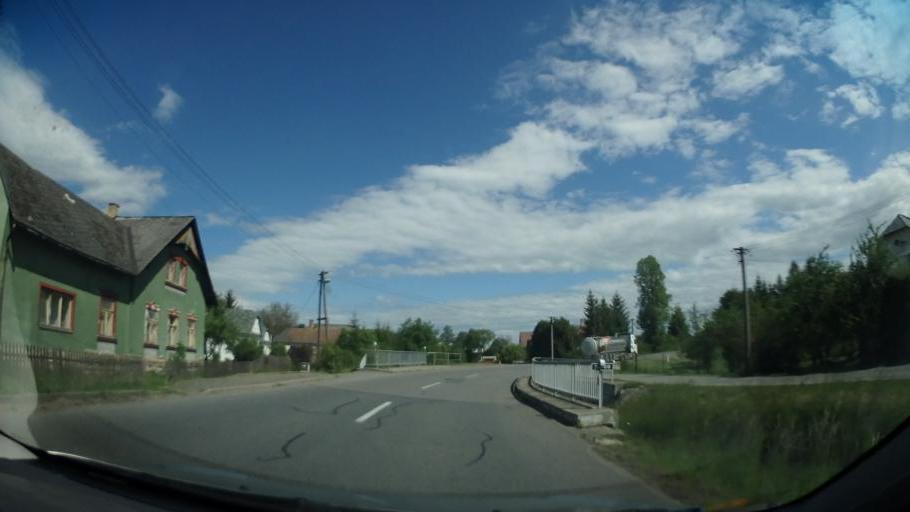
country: CZ
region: Pardubicky
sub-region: Okres Svitavy
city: Moravska Trebova
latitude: 49.7315
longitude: 16.6432
